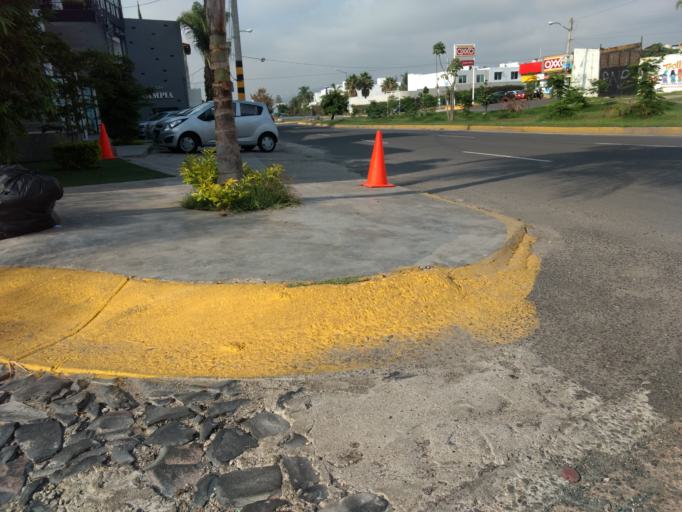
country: MX
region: Jalisco
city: Guadalajara
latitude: 20.6647
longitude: -103.4366
